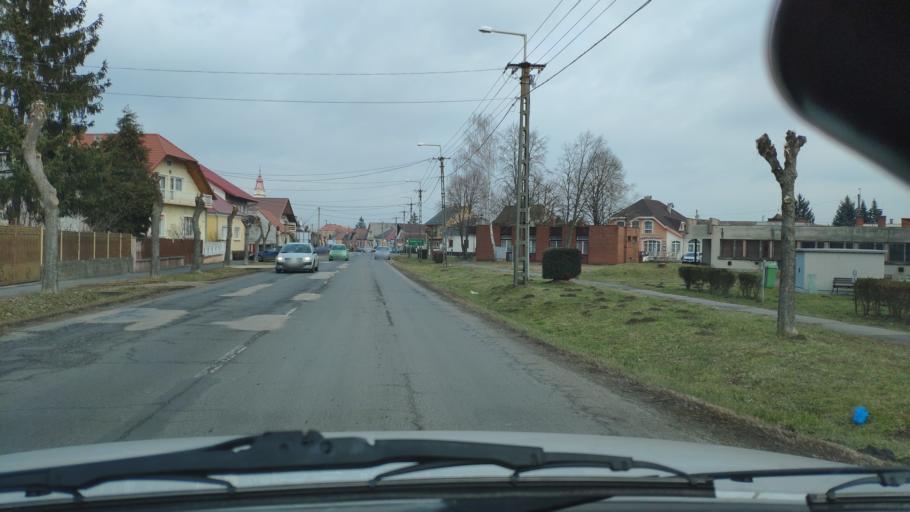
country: HU
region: Zala
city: Nagykanizsa
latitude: 46.4559
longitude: 16.9560
